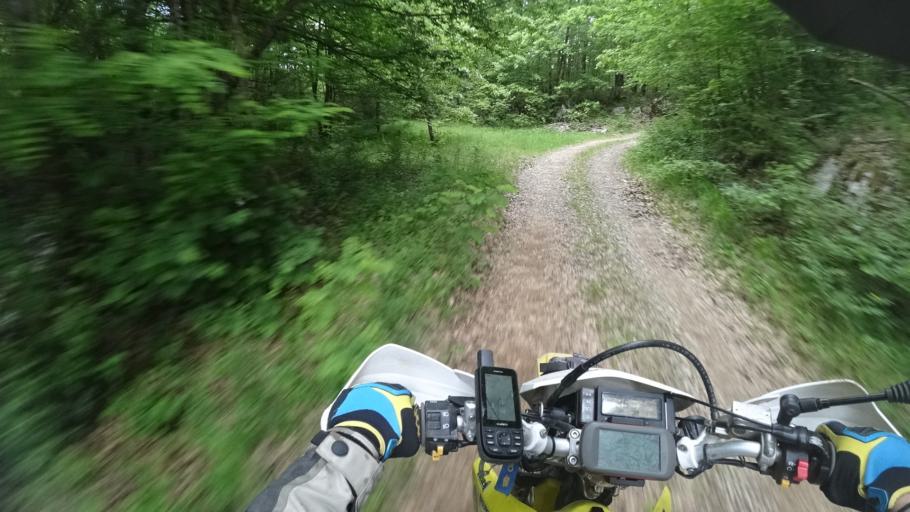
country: HR
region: Zadarska
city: Obrovac
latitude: 44.3442
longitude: 15.6502
